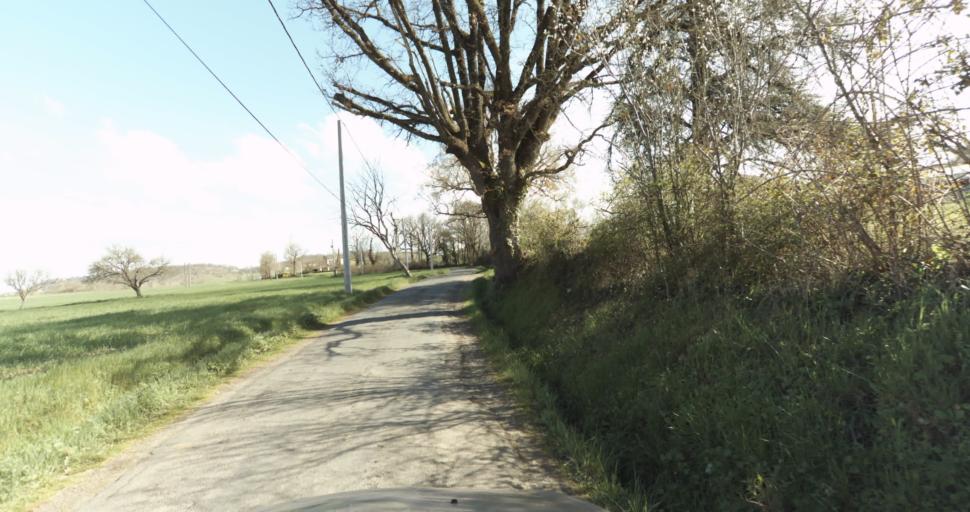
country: FR
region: Midi-Pyrenees
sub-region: Departement du Tarn
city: Puygouzon
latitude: 43.8870
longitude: 2.1835
